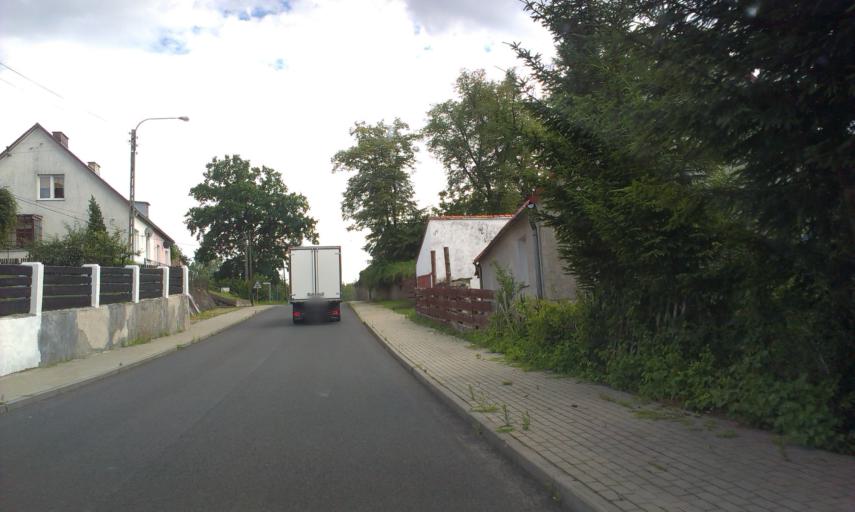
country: PL
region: Greater Poland Voivodeship
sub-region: Powiat zlotowski
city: Okonek
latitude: 53.5340
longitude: 16.9529
